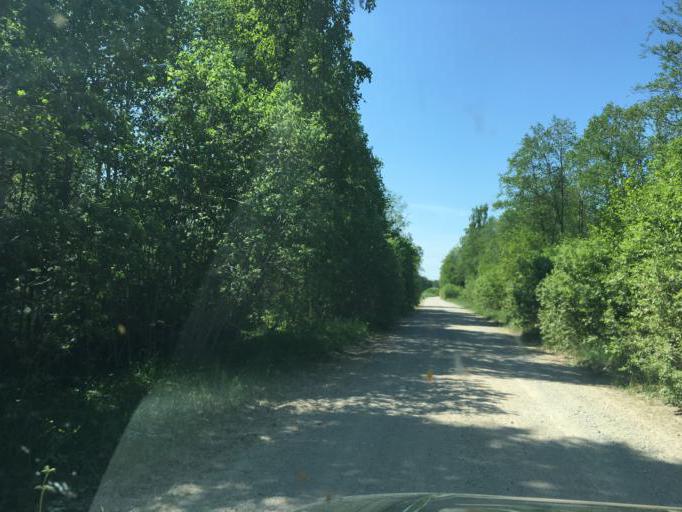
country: LV
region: Talsu Rajons
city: Valdemarpils
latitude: 57.4209
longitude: 22.7090
